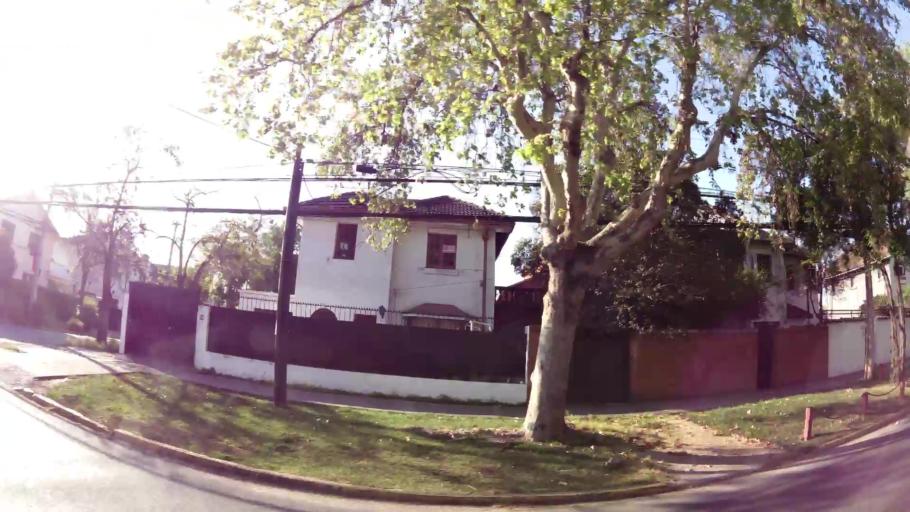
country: CL
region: Santiago Metropolitan
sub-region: Provincia de Santiago
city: Villa Presidente Frei, Nunoa, Santiago, Chile
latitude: -33.4489
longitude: -70.6072
